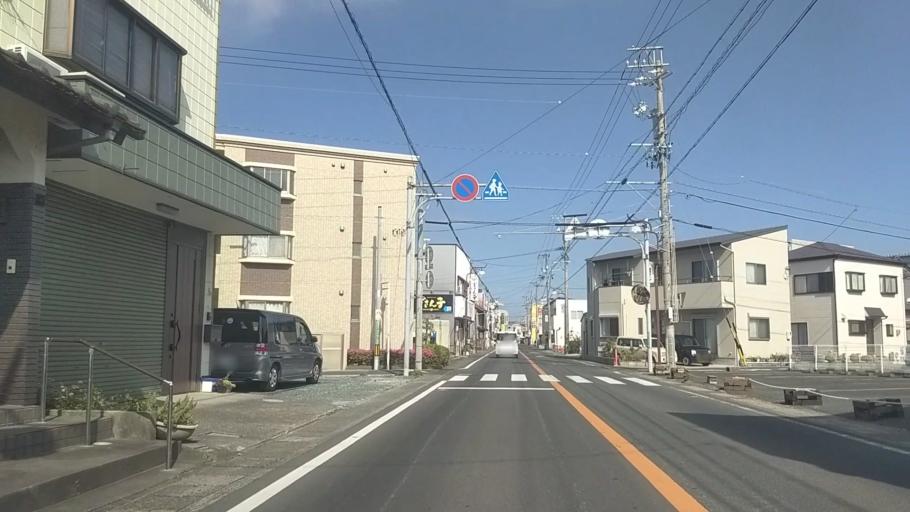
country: JP
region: Shizuoka
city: Hamamatsu
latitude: 34.7054
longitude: 137.7505
